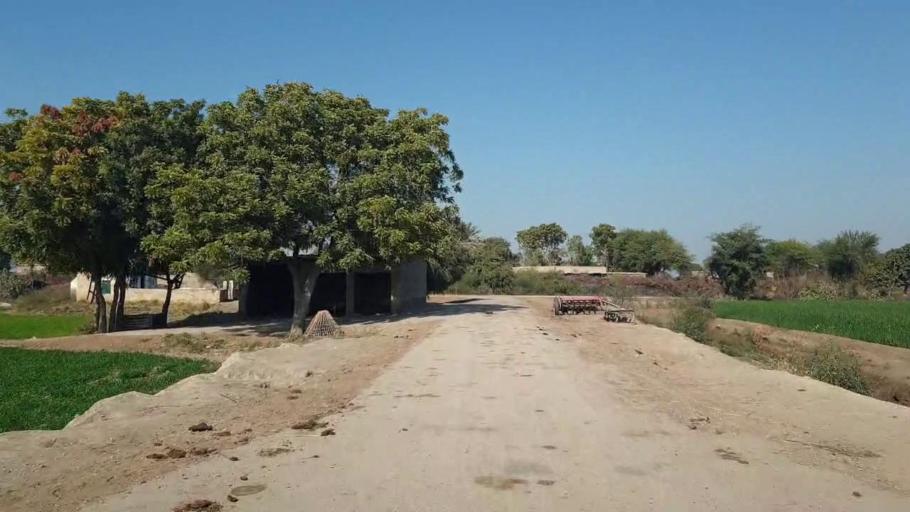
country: PK
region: Sindh
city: Shahdadpur
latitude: 25.9615
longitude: 68.6406
